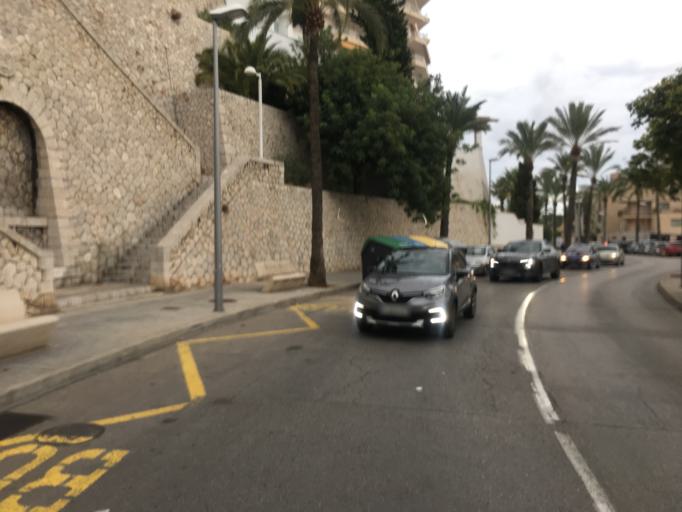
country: ES
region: Balearic Islands
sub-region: Illes Balears
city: Palma
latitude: 39.5525
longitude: 2.6081
